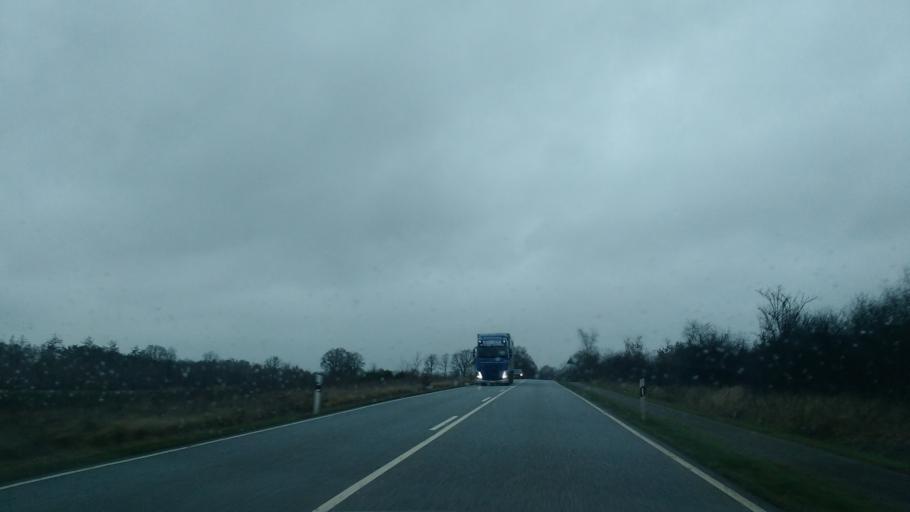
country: DE
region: Schleswig-Holstein
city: Silzen
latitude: 54.0466
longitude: 9.6207
